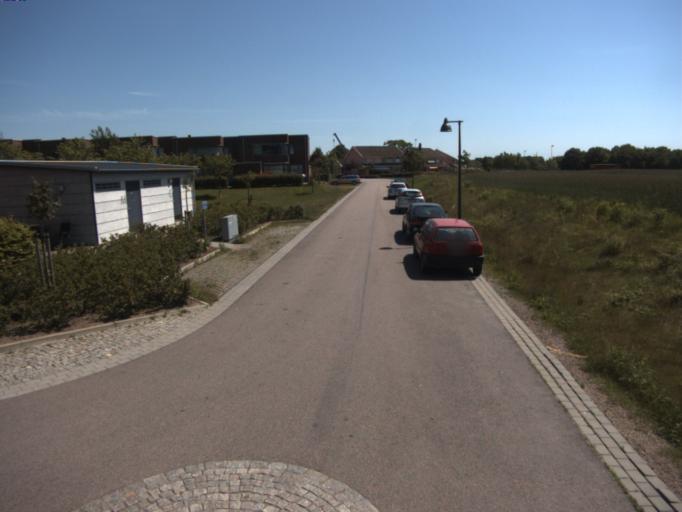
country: SE
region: Skane
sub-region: Helsingborg
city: Rydeback
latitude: 56.0042
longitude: 12.7514
